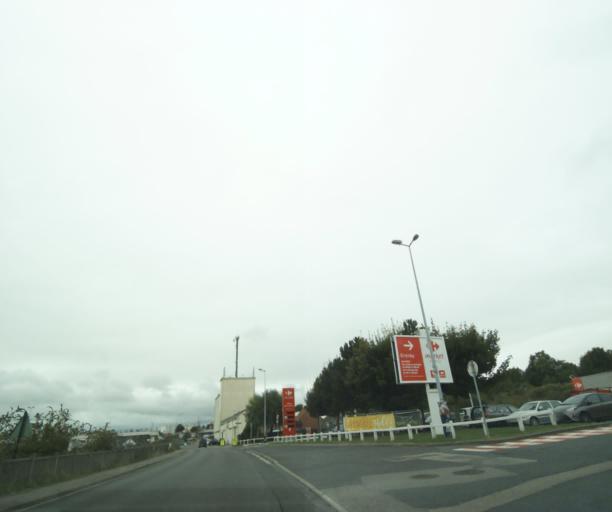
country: FR
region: Nord-Pas-de-Calais
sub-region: Departement du Pas-de-Calais
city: Etaples
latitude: 50.5152
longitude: 1.6453
